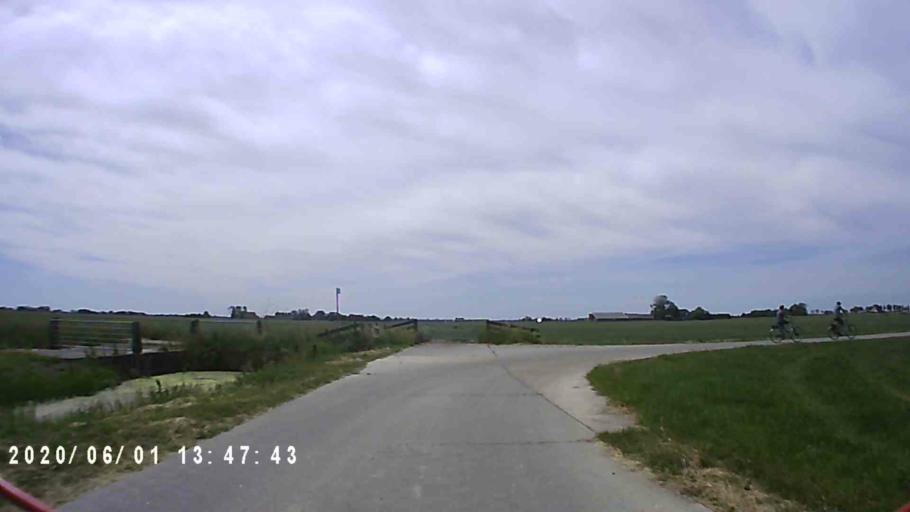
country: NL
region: Friesland
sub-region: Gemeente Littenseradiel
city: Wommels
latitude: 53.0911
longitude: 5.6232
